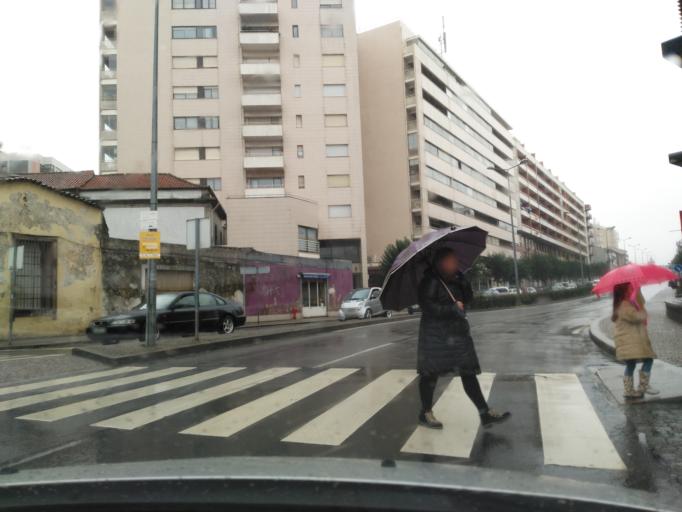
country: PT
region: Braga
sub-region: Braga
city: Braga
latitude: 41.5490
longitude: -8.4338
